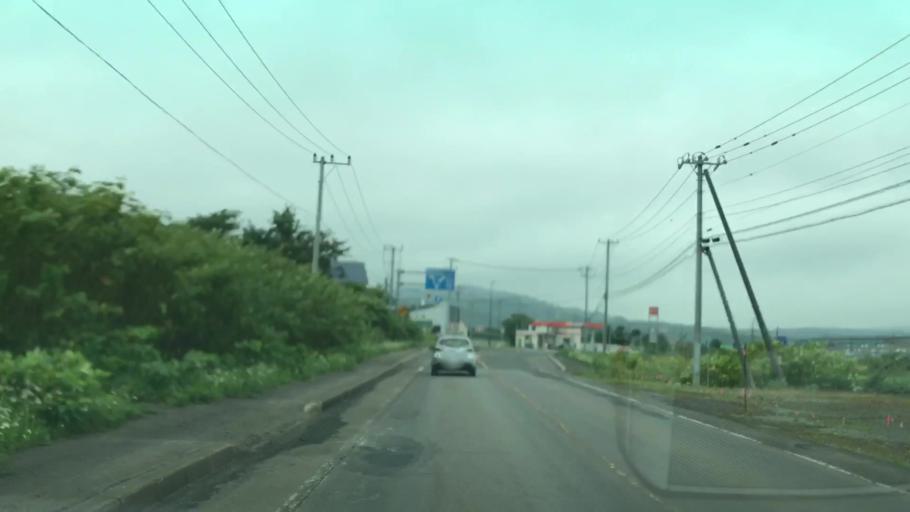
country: JP
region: Hokkaido
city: Iwanai
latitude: 42.7594
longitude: 140.2942
